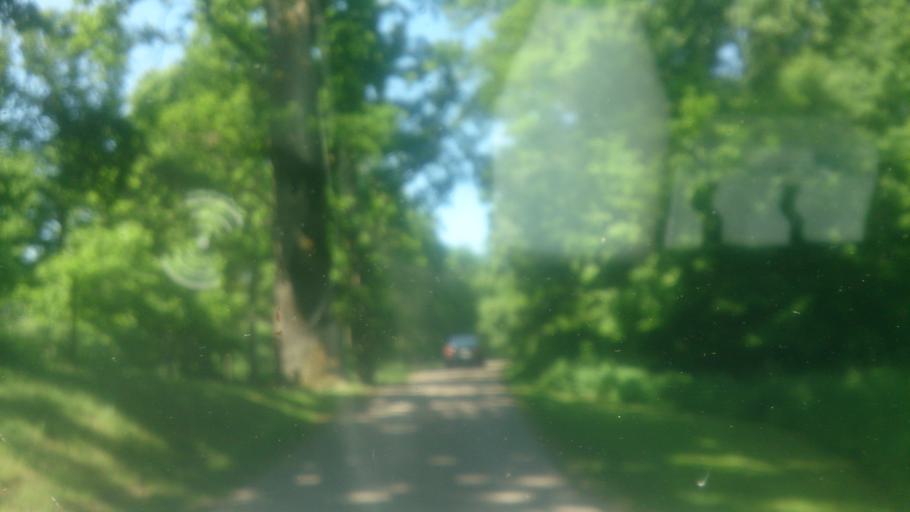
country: SE
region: OEstergoetland
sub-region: Atvidabergs Kommun
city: Atvidaberg
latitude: 58.1841
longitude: 15.9980
